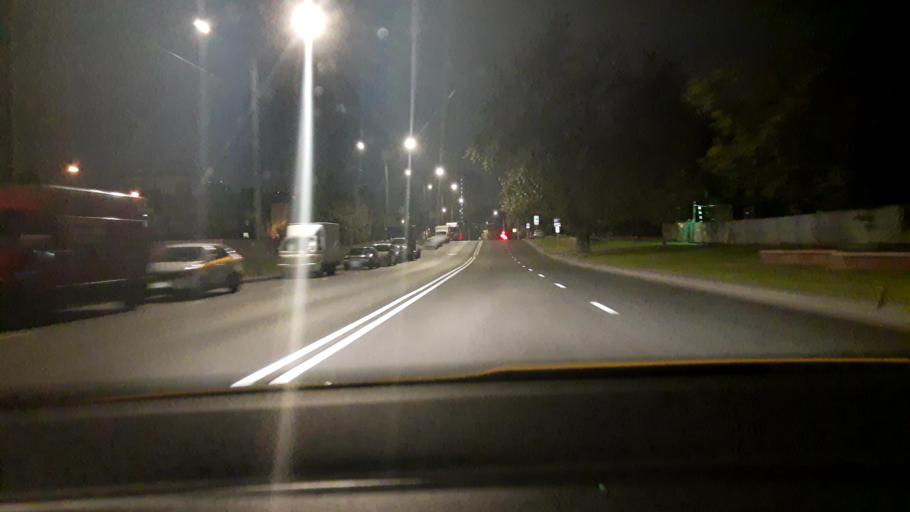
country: RU
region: Moscow
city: Lyublino
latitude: 55.6669
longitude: 37.7561
